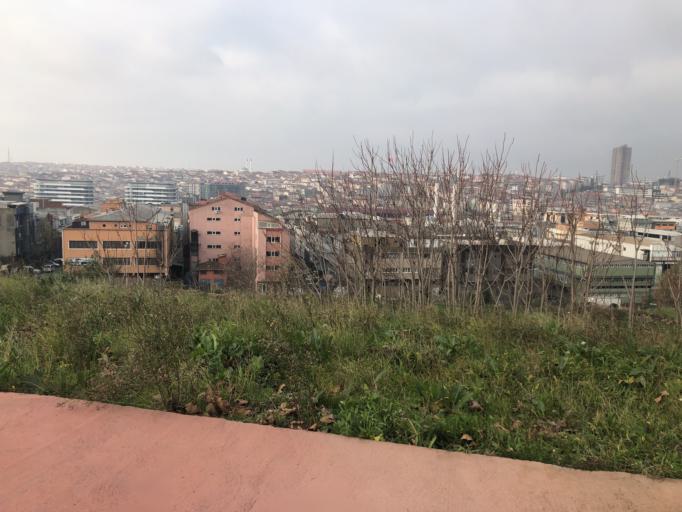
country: TR
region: Istanbul
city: merter keresteciler
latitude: 41.0237
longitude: 28.8863
